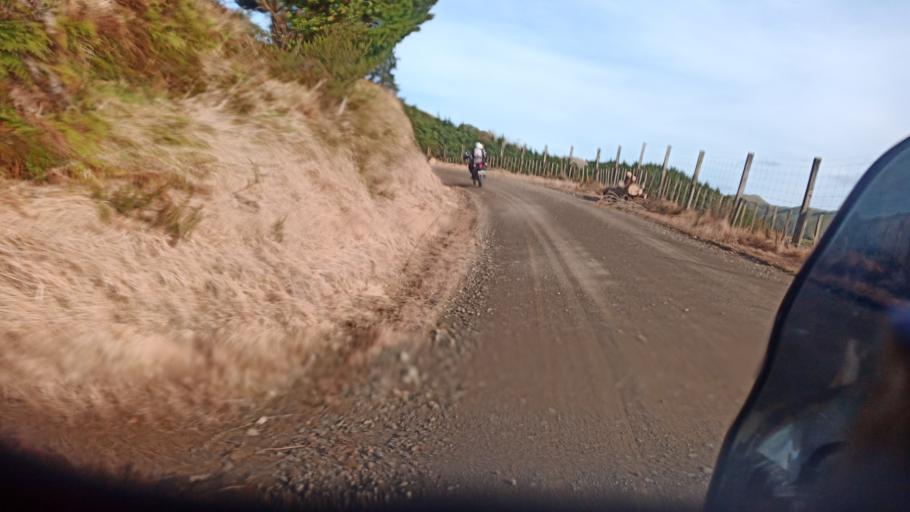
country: NZ
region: Bay of Plenty
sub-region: Opotiki District
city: Opotiki
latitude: -38.4483
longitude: 177.5392
